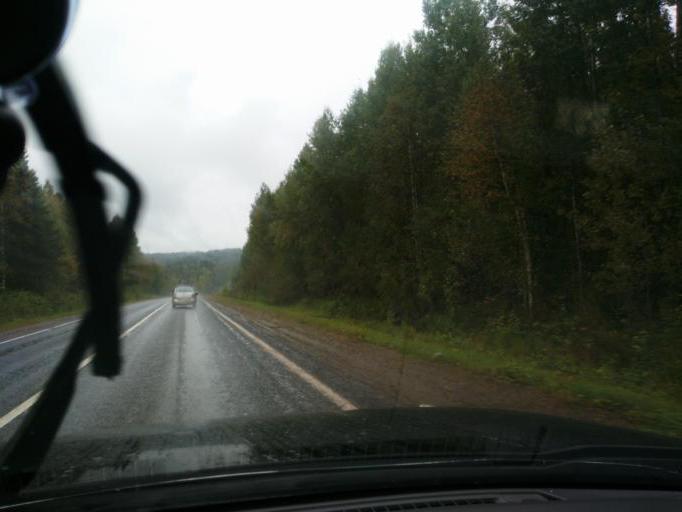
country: RU
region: Perm
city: Yugo-Kamskiy
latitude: 57.6118
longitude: 55.6378
